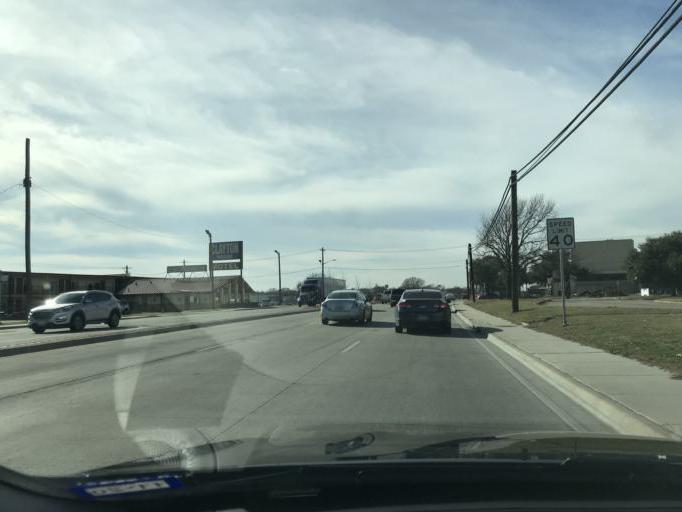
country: US
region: Texas
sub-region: Denton County
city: Denton
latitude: 33.2297
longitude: -97.1433
